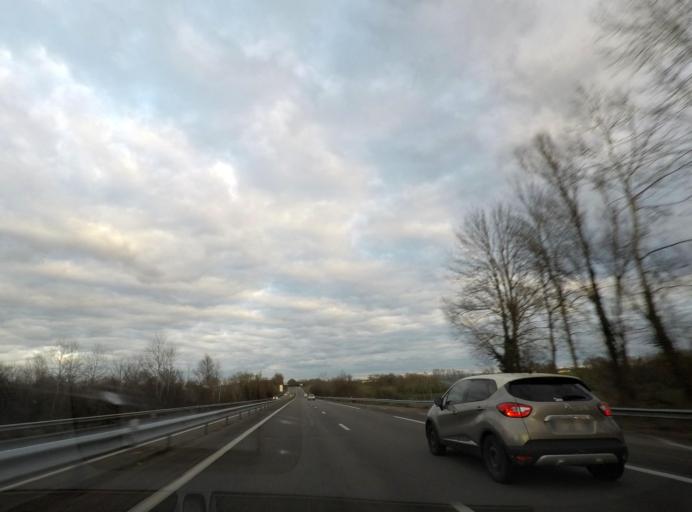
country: FR
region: Rhone-Alpes
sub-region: Departement de l'Ain
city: Mezeriat
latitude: 46.2704
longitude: 5.0473
